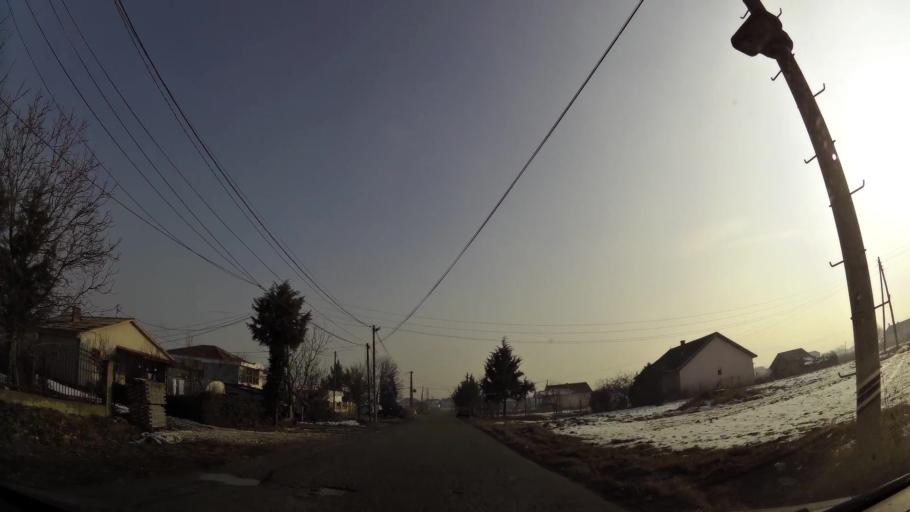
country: MK
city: Kadino
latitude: 41.9627
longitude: 21.5991
